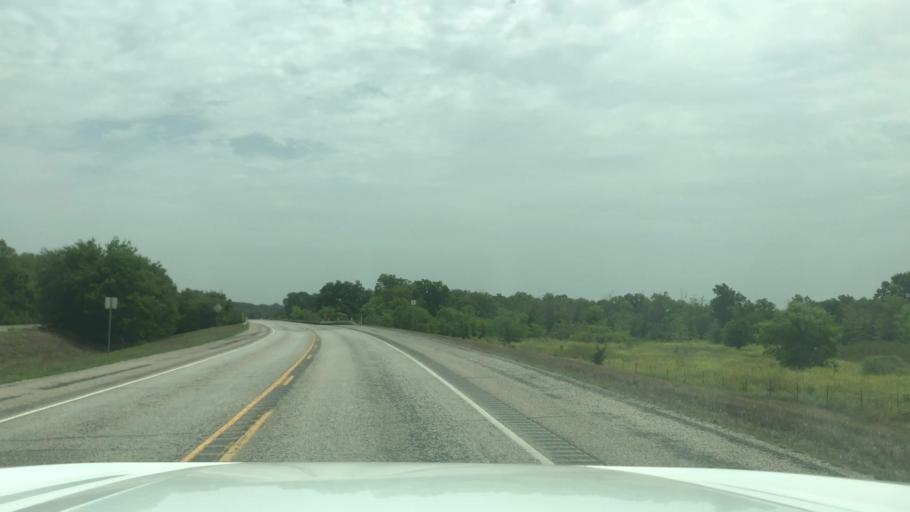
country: US
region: Texas
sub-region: Hamilton County
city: Hico
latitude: 32.0394
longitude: -98.1129
